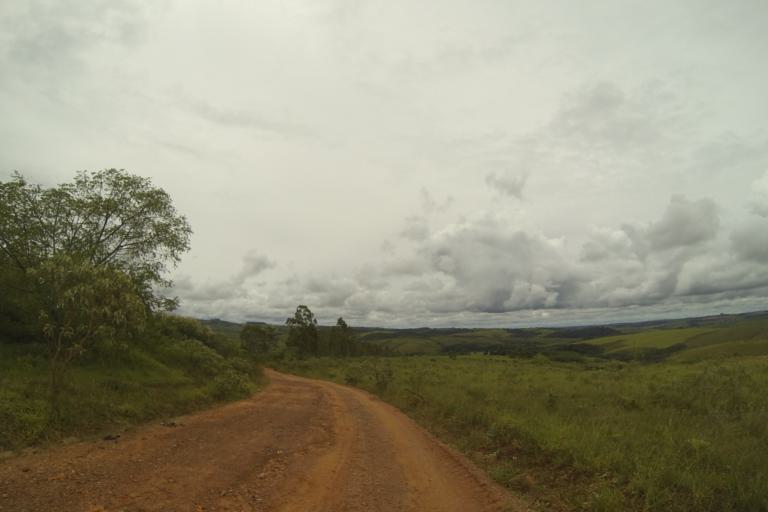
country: BR
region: Minas Gerais
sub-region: Ibia
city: Ibia
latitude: -19.6843
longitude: -46.6810
